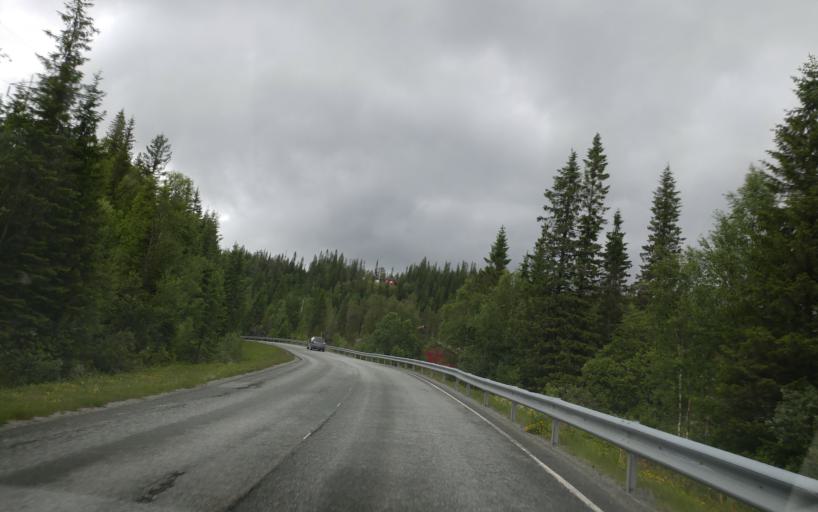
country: NO
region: Sor-Trondelag
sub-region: Selbu
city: Mebonden
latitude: 63.3359
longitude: 11.0933
